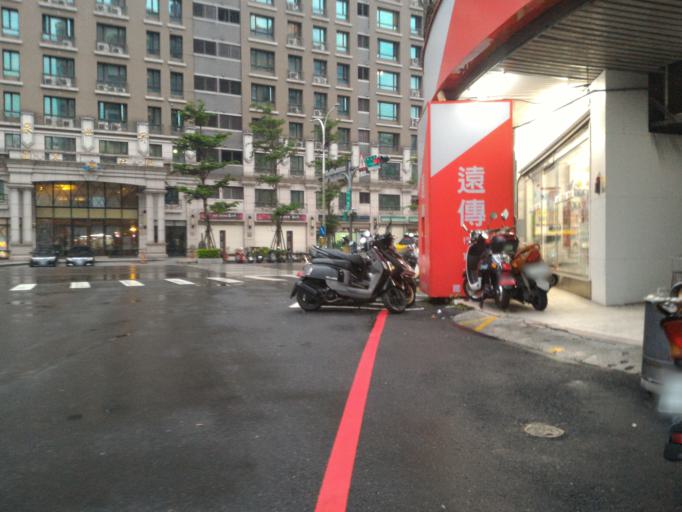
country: TW
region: Taipei
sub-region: Taipei
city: Banqiao
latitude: 24.9831
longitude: 121.4119
